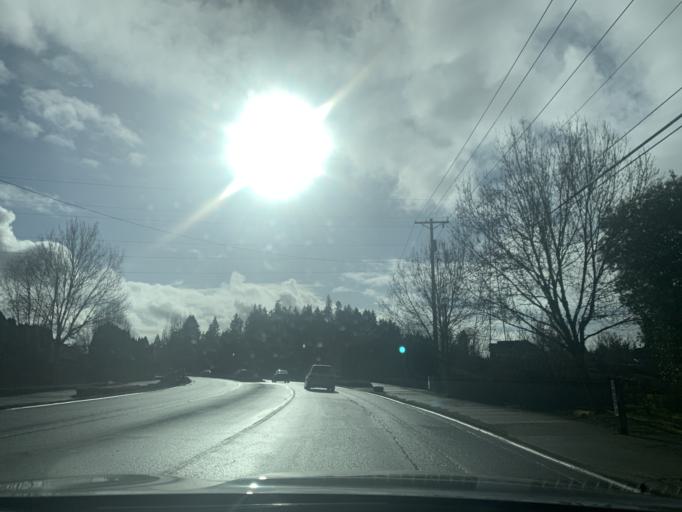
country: US
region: Oregon
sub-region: Washington County
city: Sherwood
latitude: 45.3735
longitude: -122.8567
